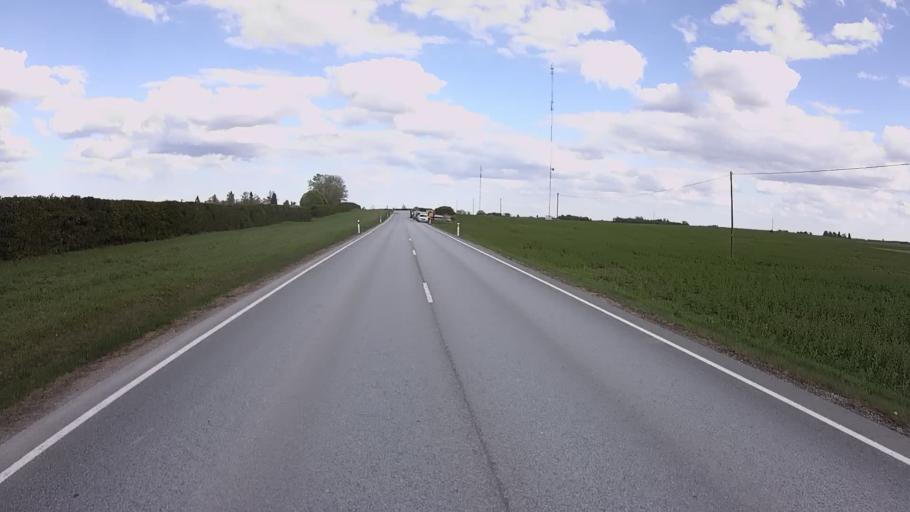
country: EE
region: Jogevamaa
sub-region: Jogeva linn
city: Jogeva
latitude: 58.8233
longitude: 26.6262
